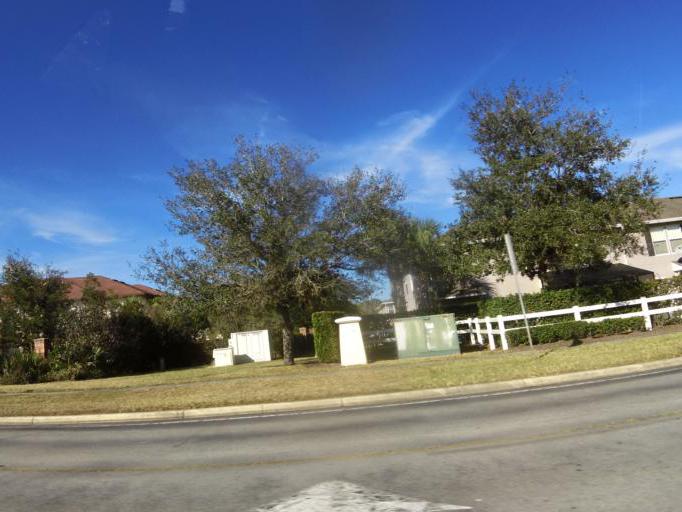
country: US
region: Florida
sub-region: Saint Johns County
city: Saint Augustine
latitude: 29.9248
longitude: -81.4059
